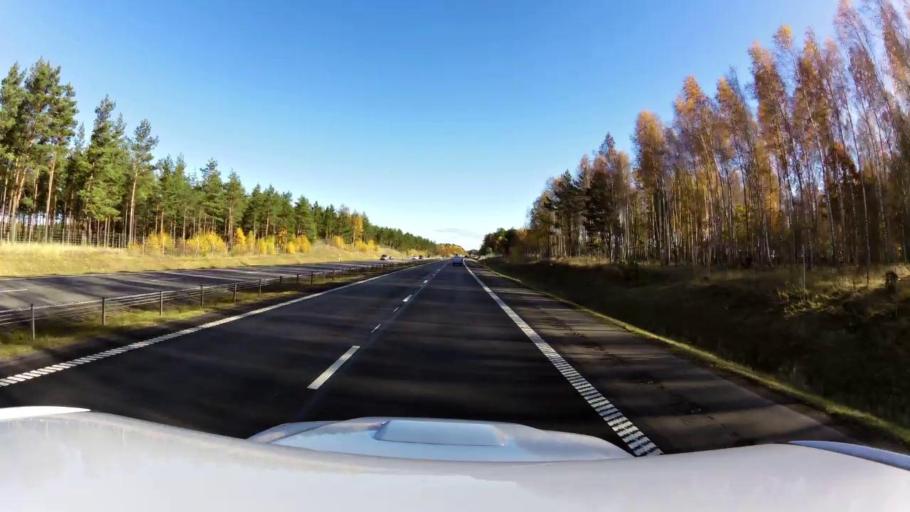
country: SE
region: OEstergoetland
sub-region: Linkopings Kommun
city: Vikingstad
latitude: 58.3848
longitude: 15.3722
